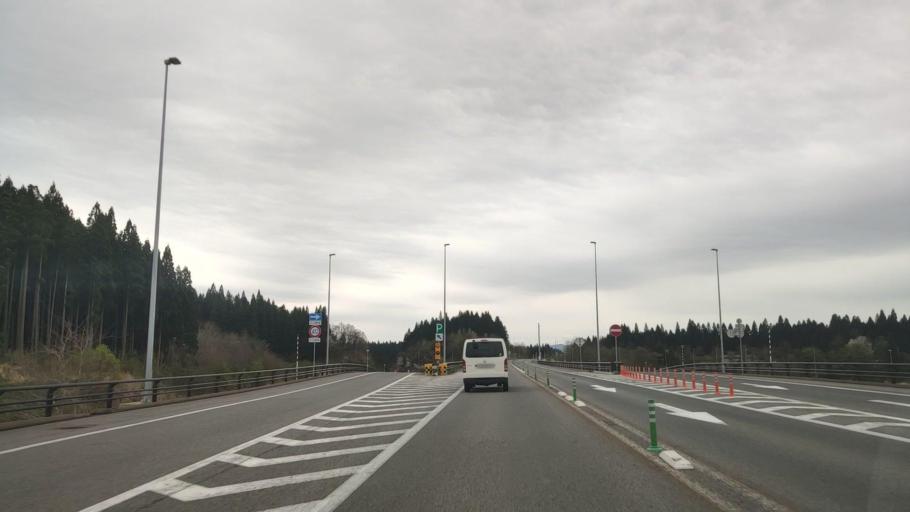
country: JP
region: Akita
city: Odate
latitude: 40.3129
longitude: 140.5790
